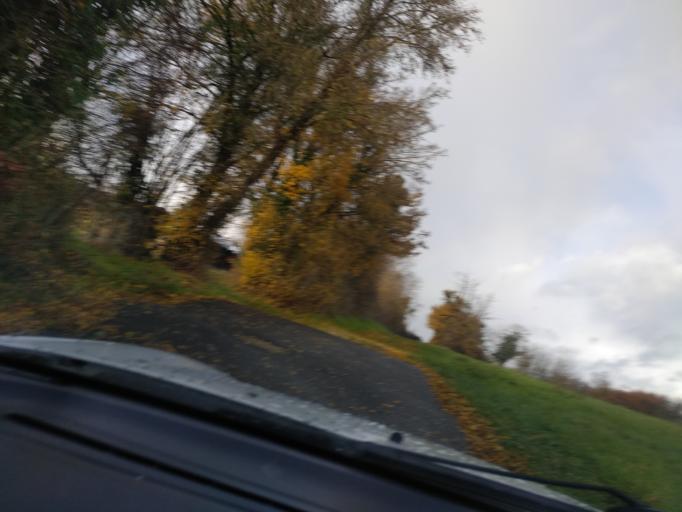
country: FR
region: Bourgogne
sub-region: Departement de Saone-et-Loire
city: Saint-Leger-sur-Dheune
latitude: 46.8401
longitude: 4.6672
